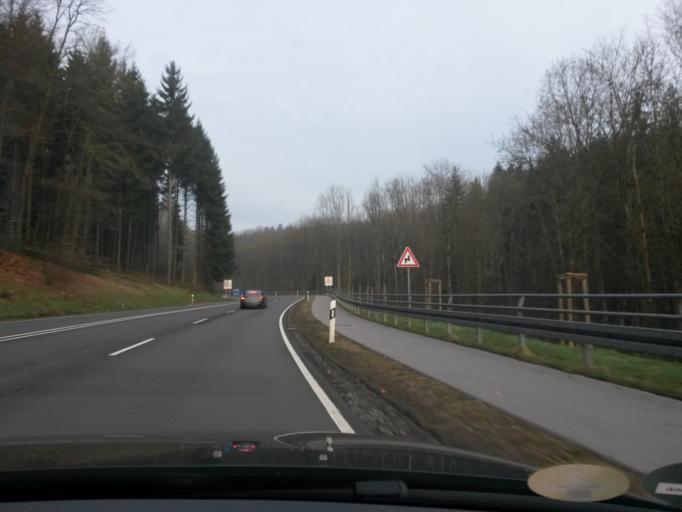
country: DE
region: North Rhine-Westphalia
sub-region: Regierungsbezirk Arnsberg
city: Herscheid
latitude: 51.1881
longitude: 7.7090
